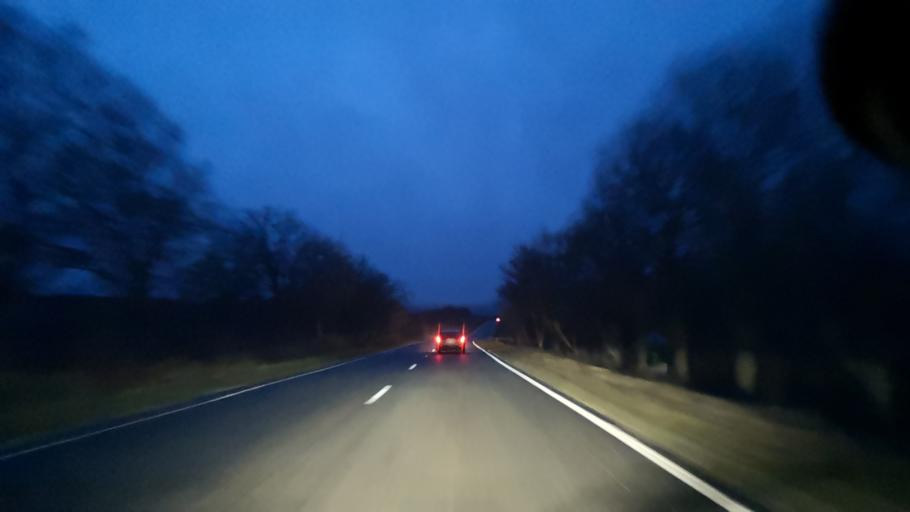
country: MD
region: Orhei
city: Orhei
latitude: 47.4830
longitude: 28.7912
